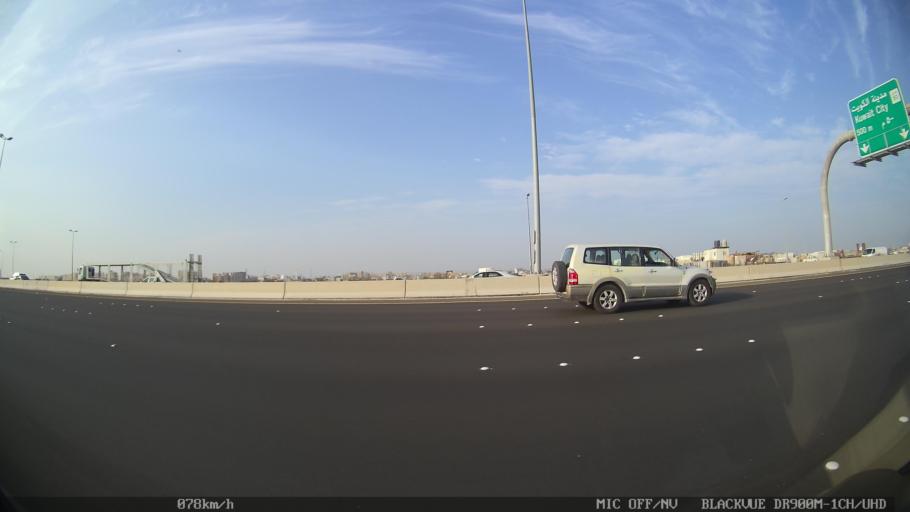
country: KW
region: Al Farwaniyah
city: Janub as Surrah
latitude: 29.2605
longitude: 47.9787
